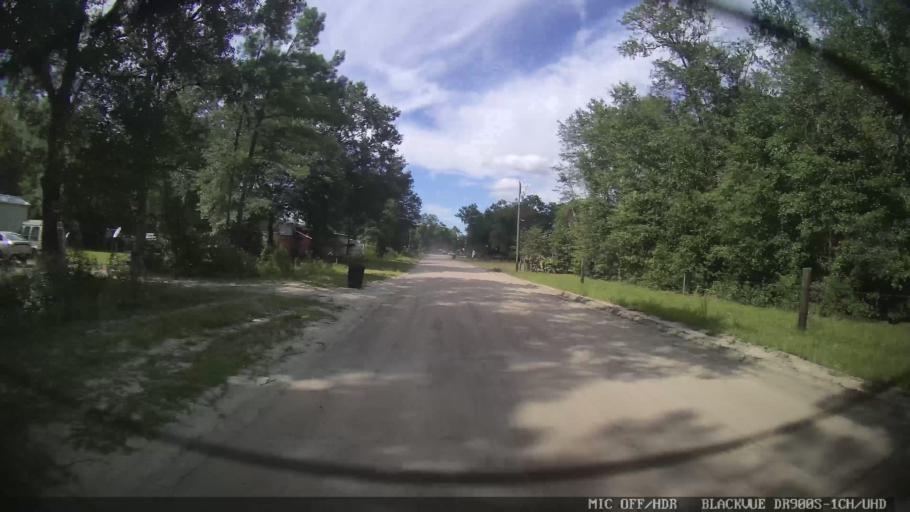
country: US
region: Florida
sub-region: Hamilton County
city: Jasper
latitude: 30.5556
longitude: -83.0885
